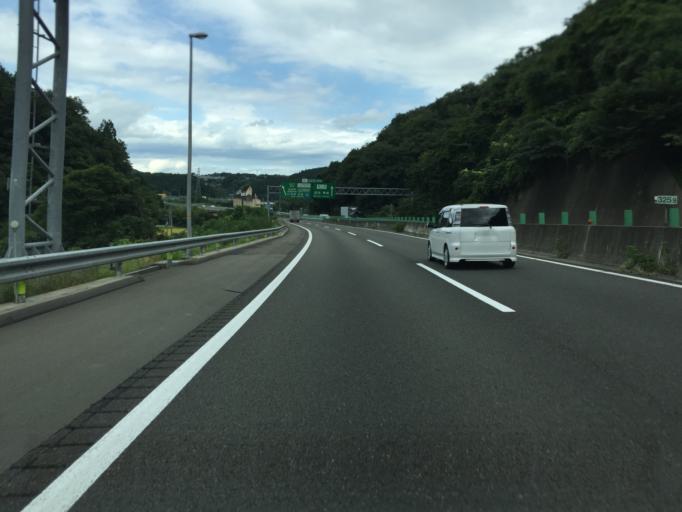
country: JP
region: Miyagi
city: Sendai
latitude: 38.2079
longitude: 140.8042
